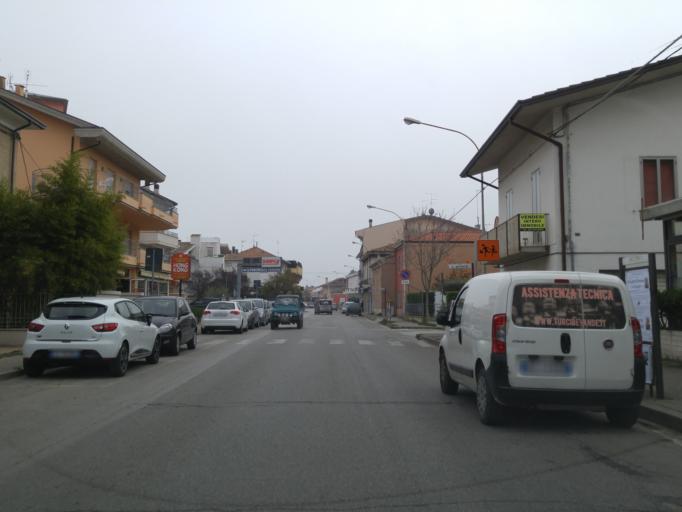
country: IT
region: The Marches
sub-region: Provincia di Pesaro e Urbino
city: Gabicce Mare
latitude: 43.9610
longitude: 12.7472
